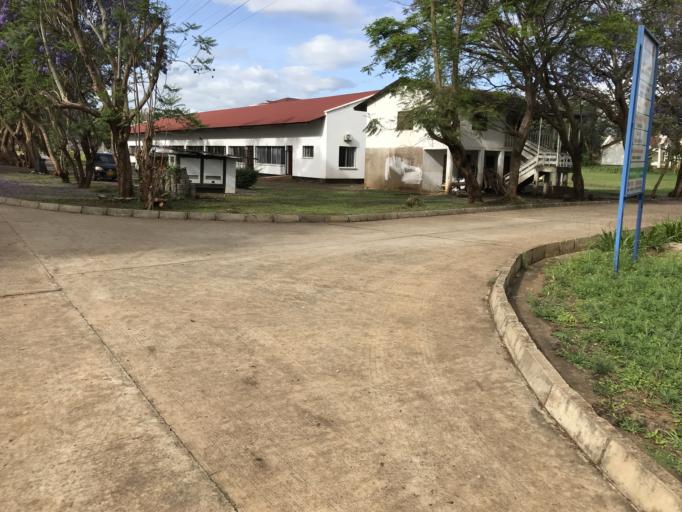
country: TZ
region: Arusha
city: Usa River
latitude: -3.4001
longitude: 36.7982
